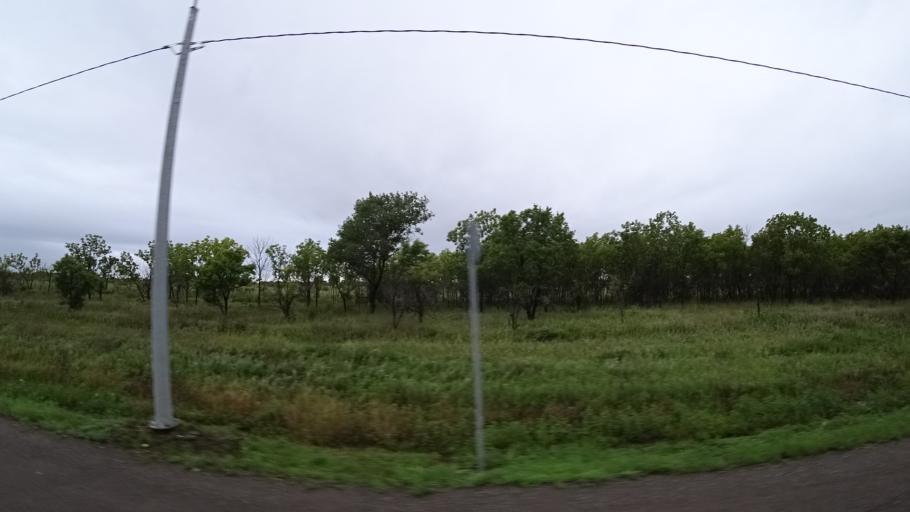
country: RU
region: Primorskiy
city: Chernigovka
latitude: 44.3272
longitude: 132.5721
